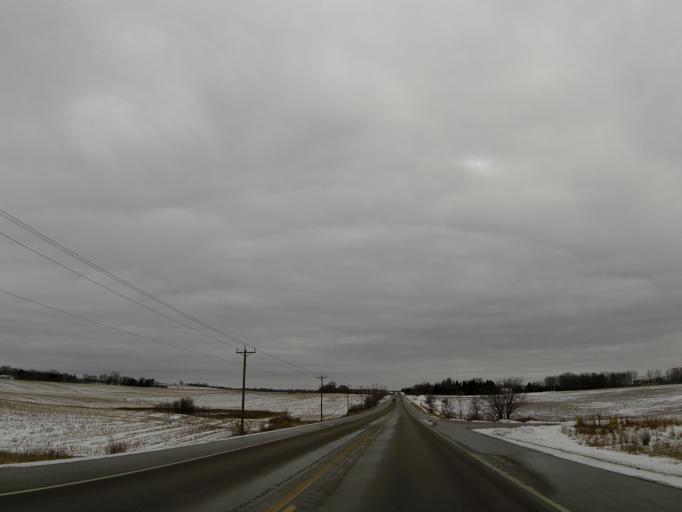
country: US
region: Minnesota
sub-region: Washington County
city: Cottage Grove
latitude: 44.8826
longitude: -92.9033
